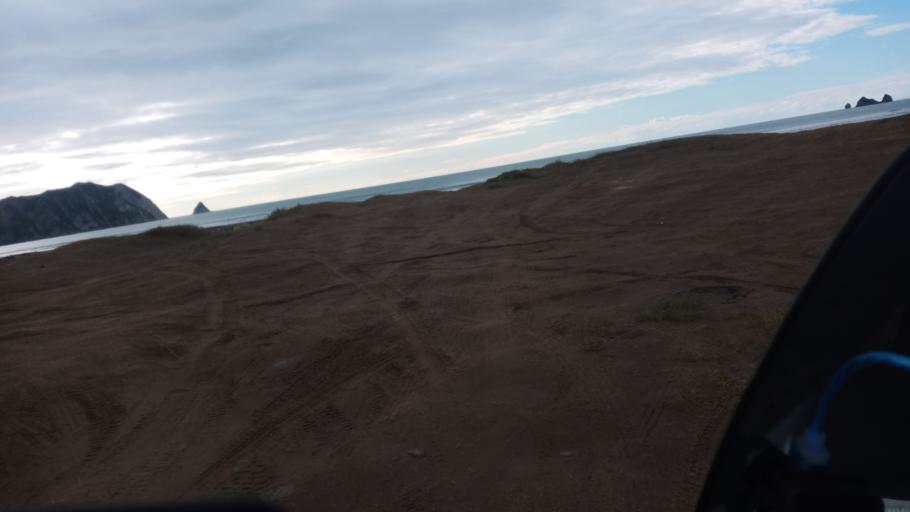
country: NZ
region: Gisborne
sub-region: Gisborne District
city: Gisborne
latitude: -38.3715
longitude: 178.3062
